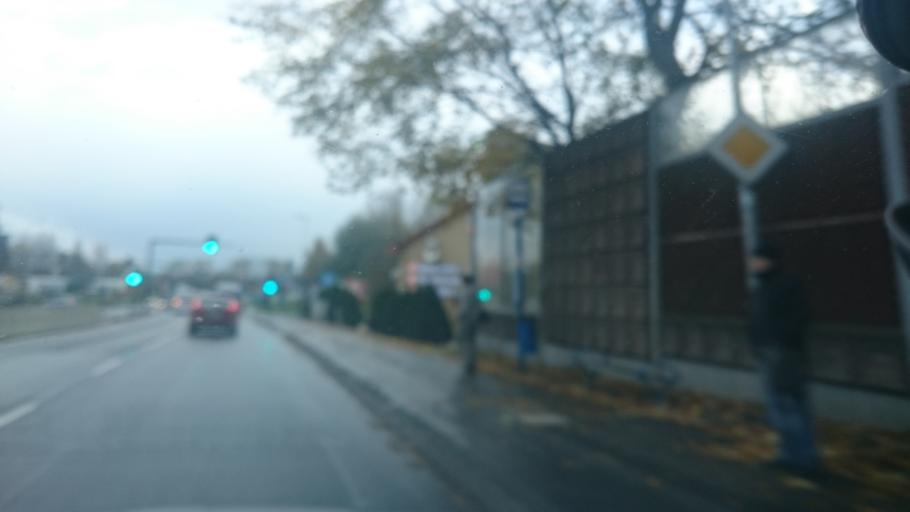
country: PL
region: Lesser Poland Voivodeship
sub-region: Krakow
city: Krakow
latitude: 50.0265
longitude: 19.9728
